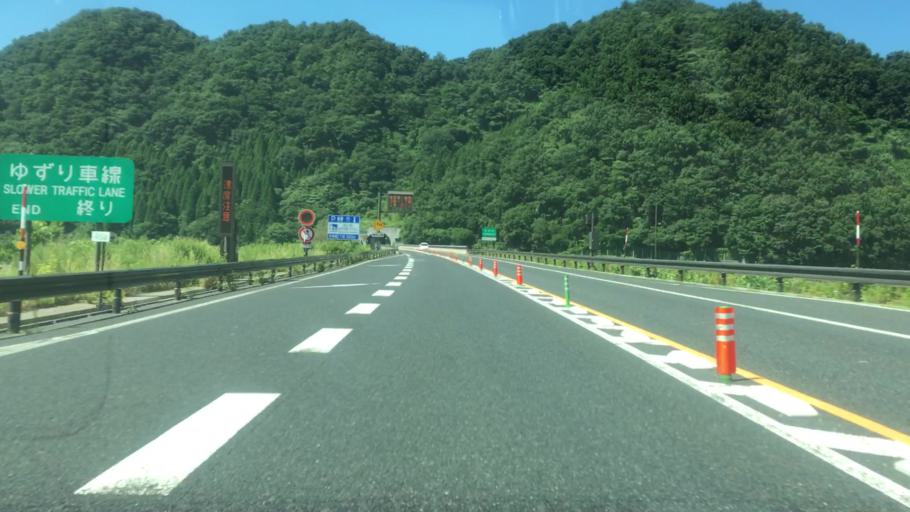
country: JP
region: Tottori
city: Tottori
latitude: 35.3778
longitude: 134.2048
